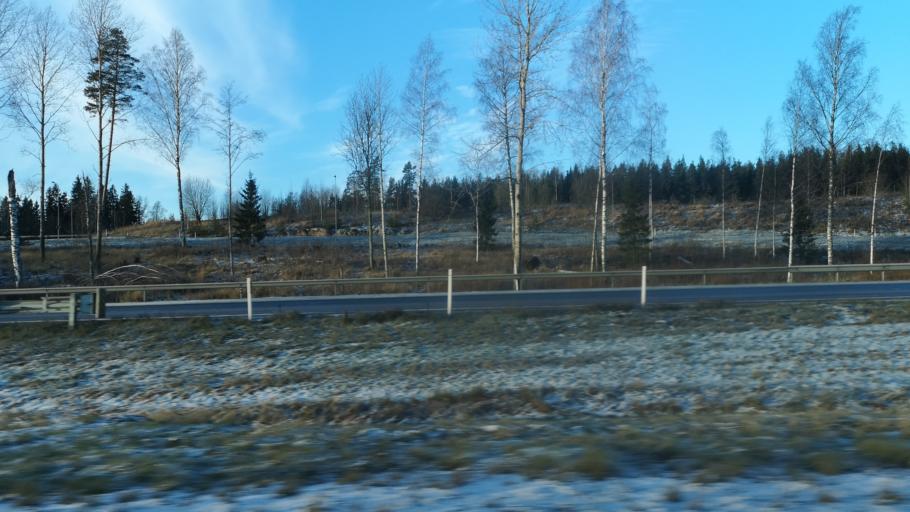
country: FI
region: Uusimaa
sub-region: Helsinki
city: Jaervenpaeae
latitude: 60.5008
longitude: 25.1364
